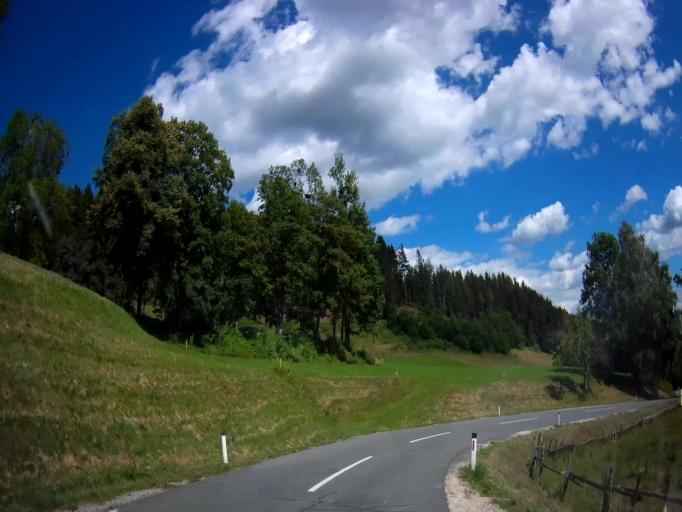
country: AT
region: Carinthia
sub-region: Politischer Bezirk Sankt Veit an der Glan
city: St. Georgen am Laengsee
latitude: 46.7238
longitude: 14.4315
